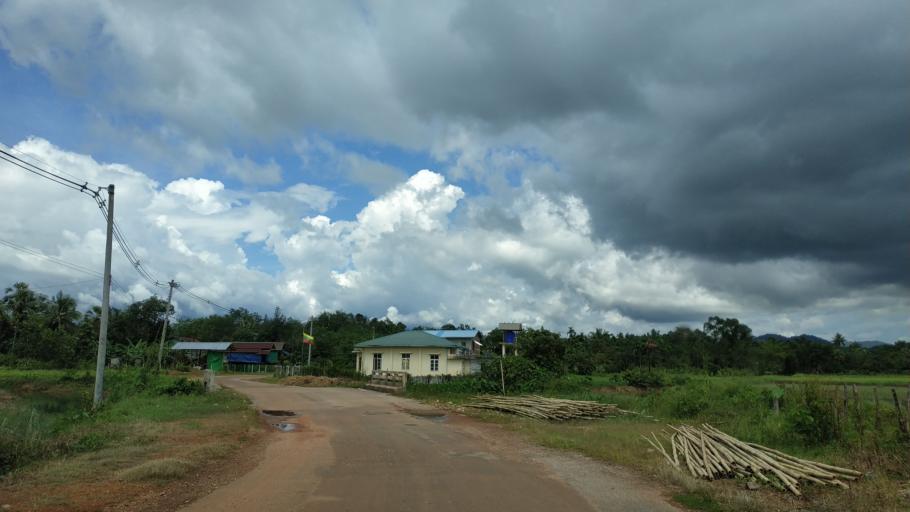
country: MM
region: Tanintharyi
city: Dawei
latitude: 14.2763
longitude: 98.1493
